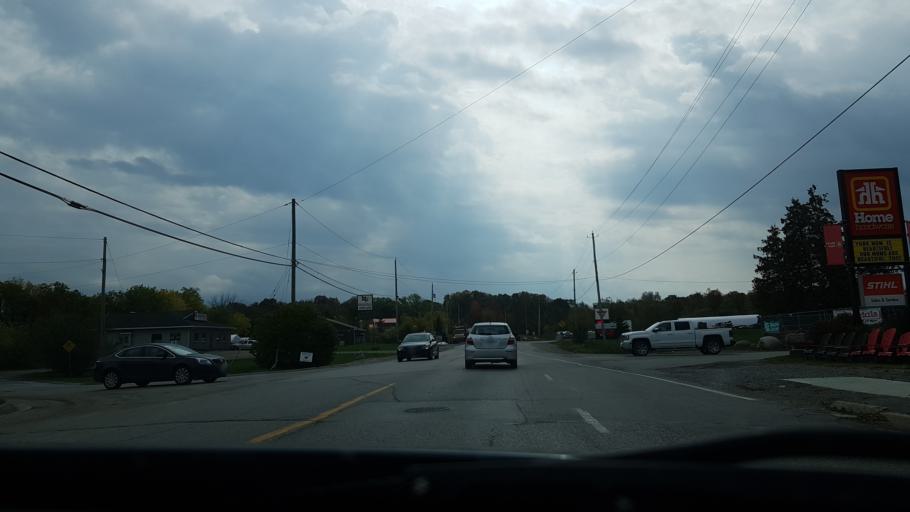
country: CA
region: Ontario
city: Omemee
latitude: 44.5291
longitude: -78.7415
